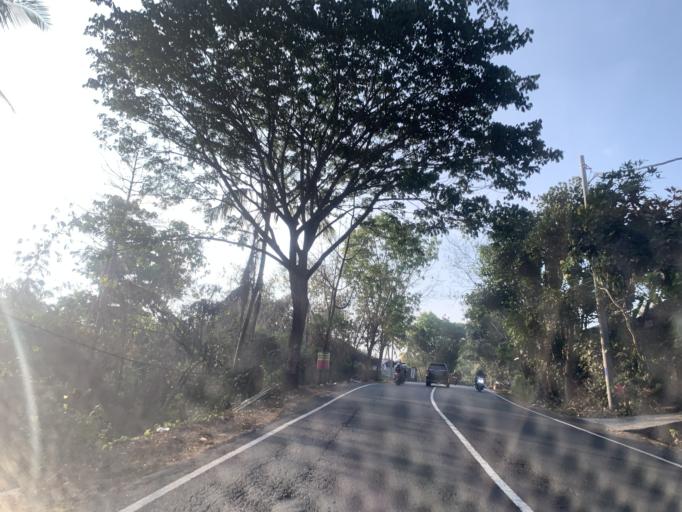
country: ID
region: Bali
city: Banjar Delodrurung
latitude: -8.5014
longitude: 115.0216
